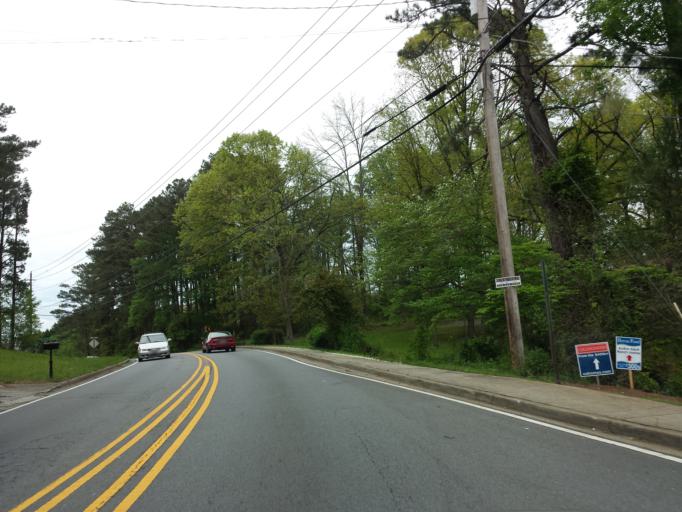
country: US
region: Georgia
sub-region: Cherokee County
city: Woodstock
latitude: 34.0434
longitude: -84.4818
